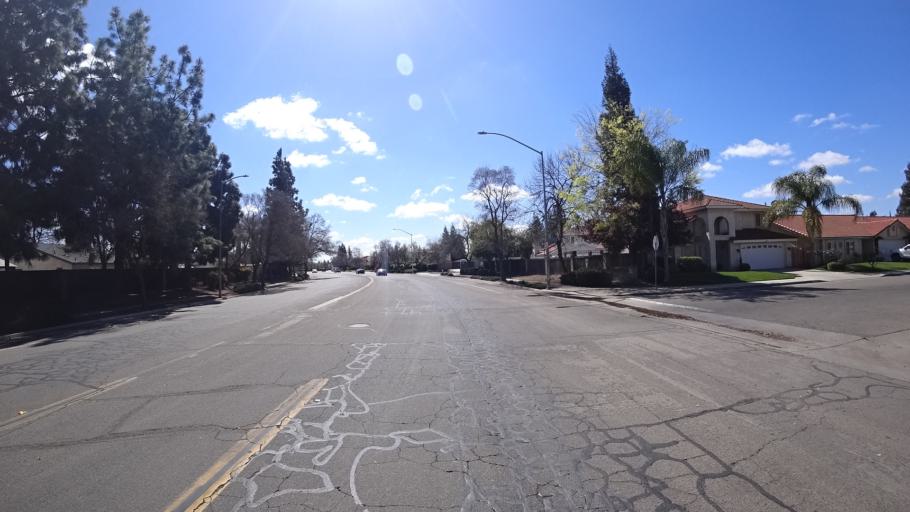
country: US
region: California
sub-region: Fresno County
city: West Park
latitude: 36.8248
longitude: -119.8897
